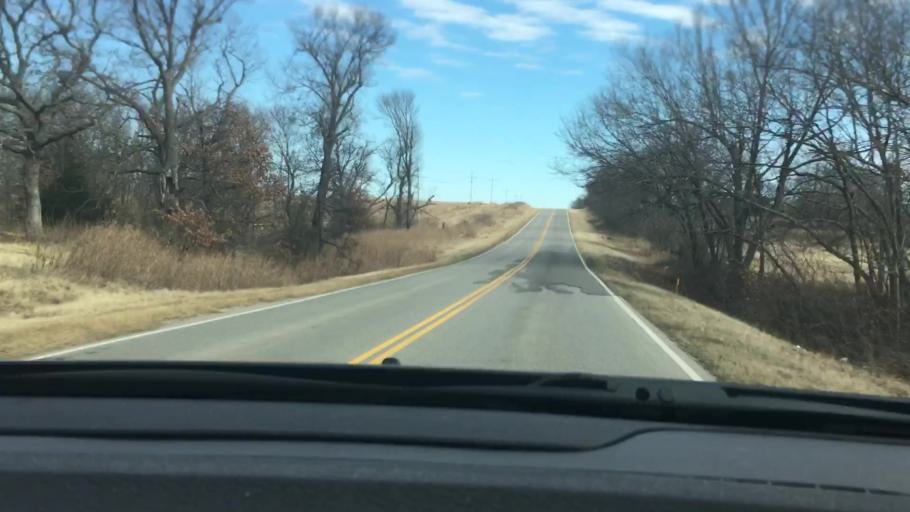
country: US
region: Oklahoma
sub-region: Garvin County
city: Stratford
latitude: 34.7968
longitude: -96.8373
